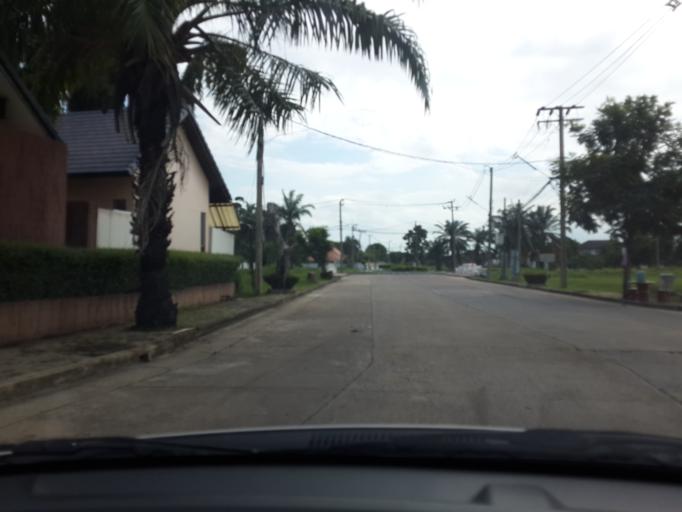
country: TH
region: Bangkok
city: Khlong Sam Wa
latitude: 13.8412
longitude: 100.7642
